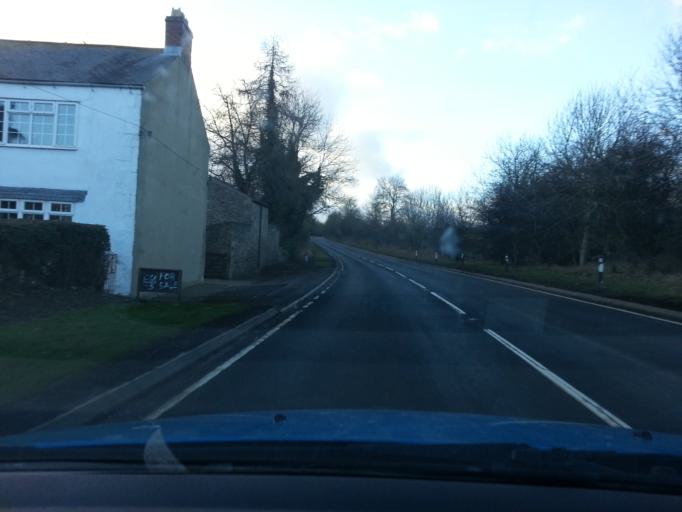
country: GB
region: England
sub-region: County Durham
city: Wolsingham
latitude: 54.7279
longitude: -1.9207
